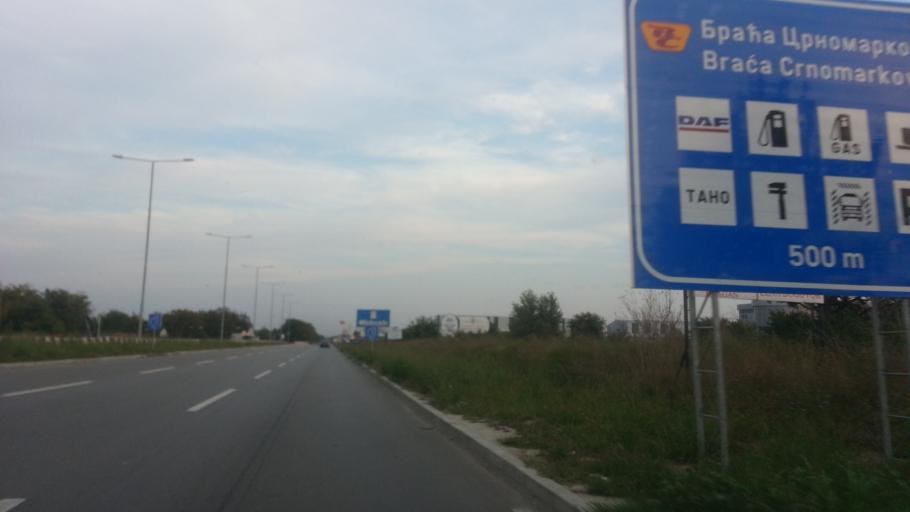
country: RS
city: Novi Banovci
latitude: 44.8869
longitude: 20.3039
